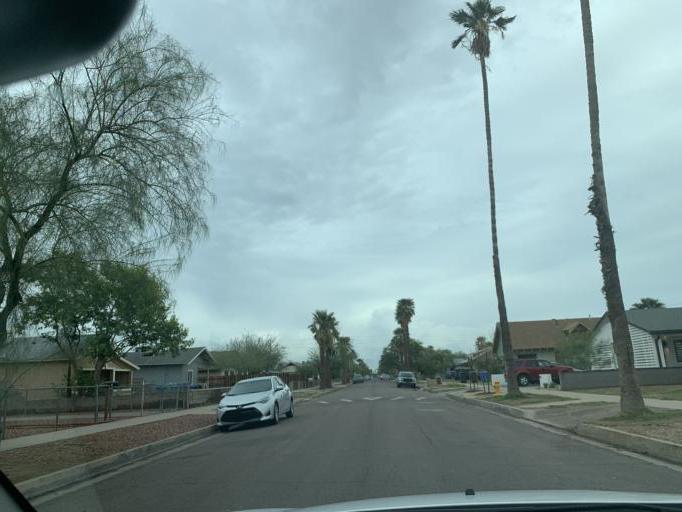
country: US
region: Arizona
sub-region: Maricopa County
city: Phoenix
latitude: 33.4568
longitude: -112.0580
